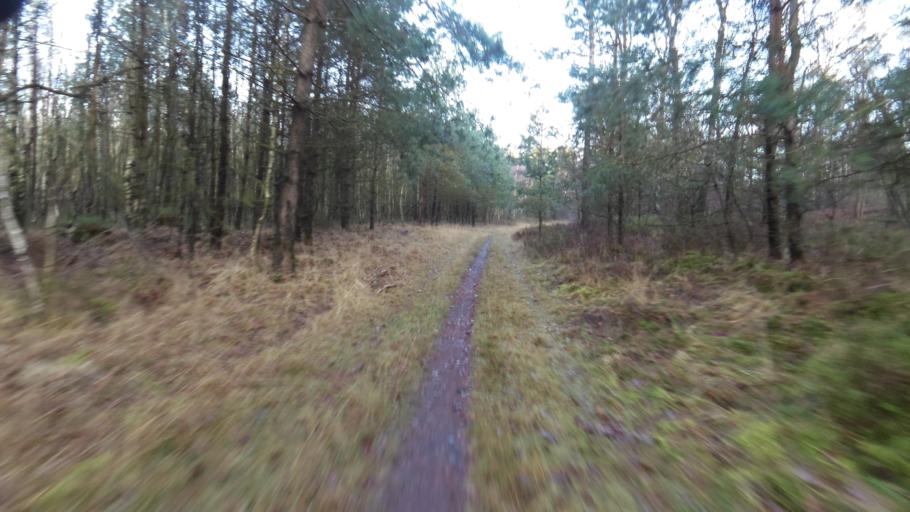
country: NL
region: Gelderland
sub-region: Gemeente Apeldoorn
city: Uddel
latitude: 52.2280
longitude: 5.8374
